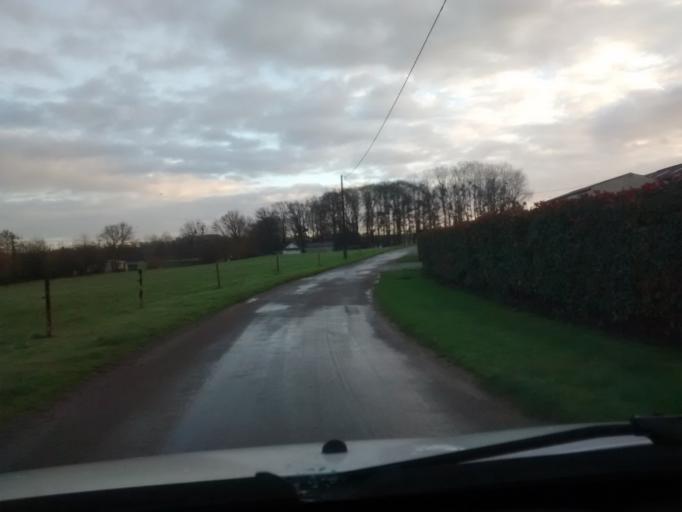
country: FR
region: Brittany
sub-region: Departement d'Ille-et-Vilaine
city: Domalain
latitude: 47.9649
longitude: -1.2559
